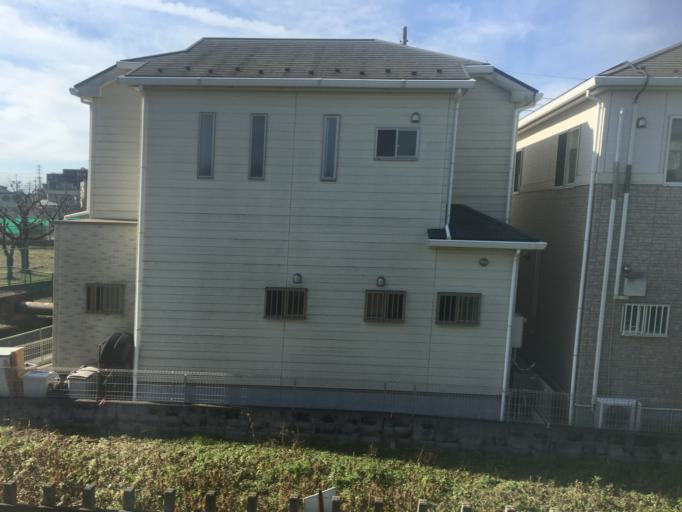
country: JP
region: Saitama
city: Kawagoe
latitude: 35.9197
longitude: 139.4703
